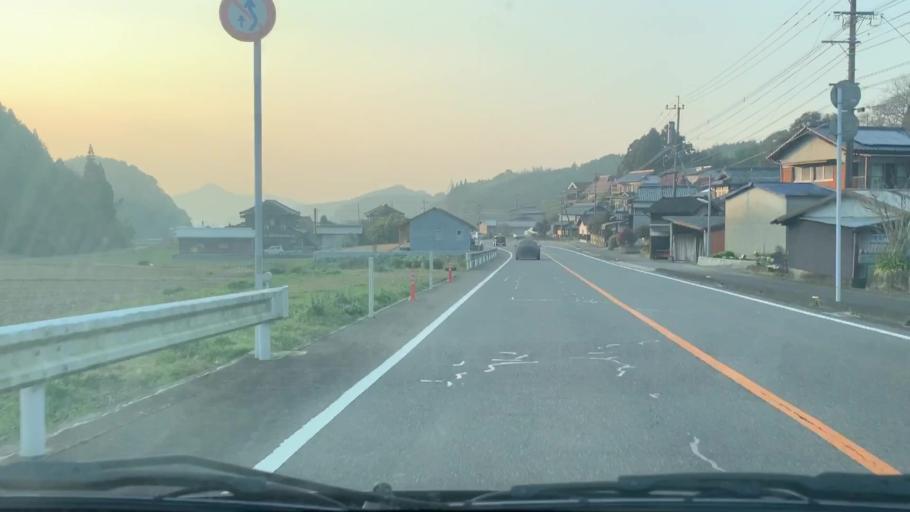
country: JP
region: Saga Prefecture
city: Takeocho-takeo
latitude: 33.2558
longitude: 130.0109
